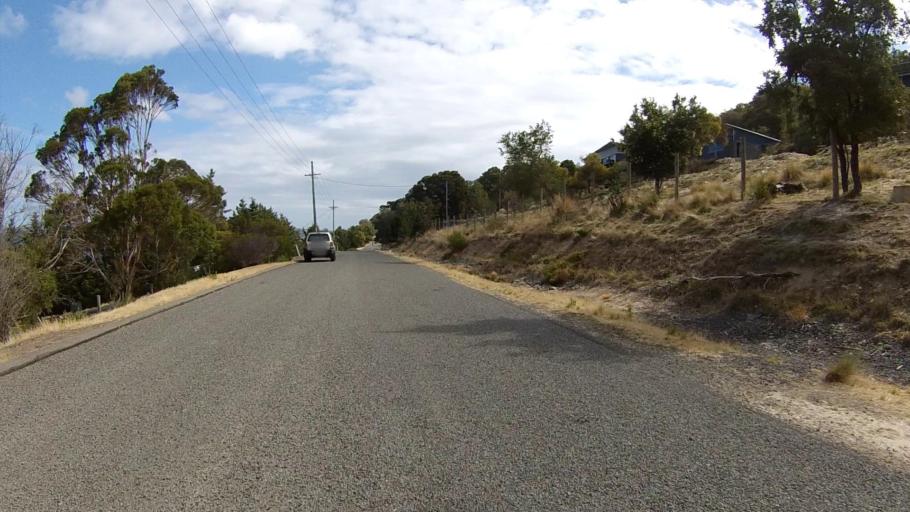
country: AU
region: Tasmania
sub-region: Clarence
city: Acton Park
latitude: -42.8809
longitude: 147.5044
